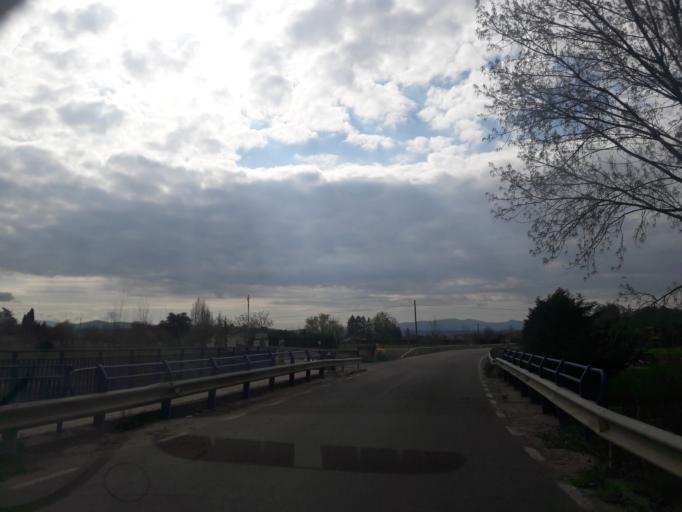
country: ES
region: Castille and Leon
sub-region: Provincia de Salamanca
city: Ciudad Rodrigo
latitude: 40.5938
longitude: -6.5168
